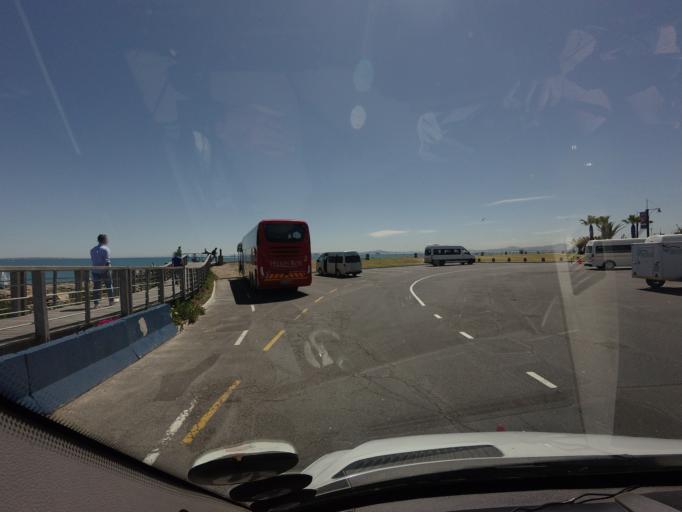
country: ZA
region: Western Cape
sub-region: City of Cape Town
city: Cape Town
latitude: -33.9020
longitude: 18.4204
